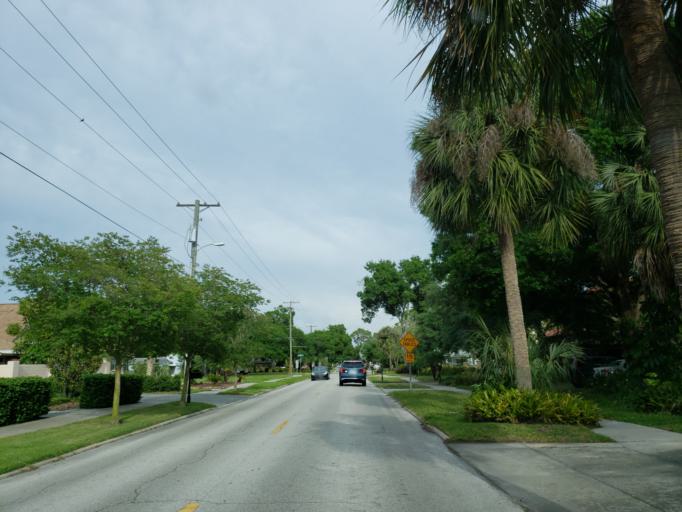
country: US
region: Florida
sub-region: Hillsborough County
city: Tampa
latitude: 27.9376
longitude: -82.5129
